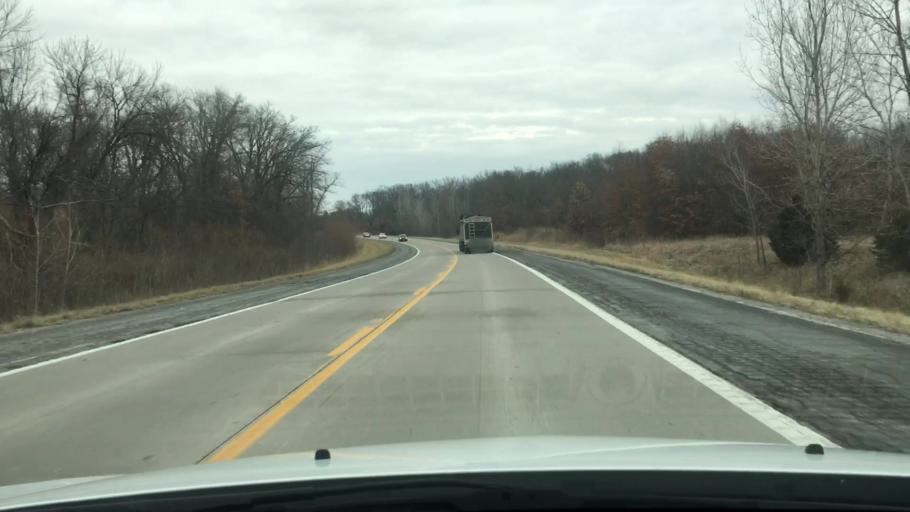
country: US
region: Missouri
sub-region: Audrain County
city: Mexico
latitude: 39.1446
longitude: -91.8458
